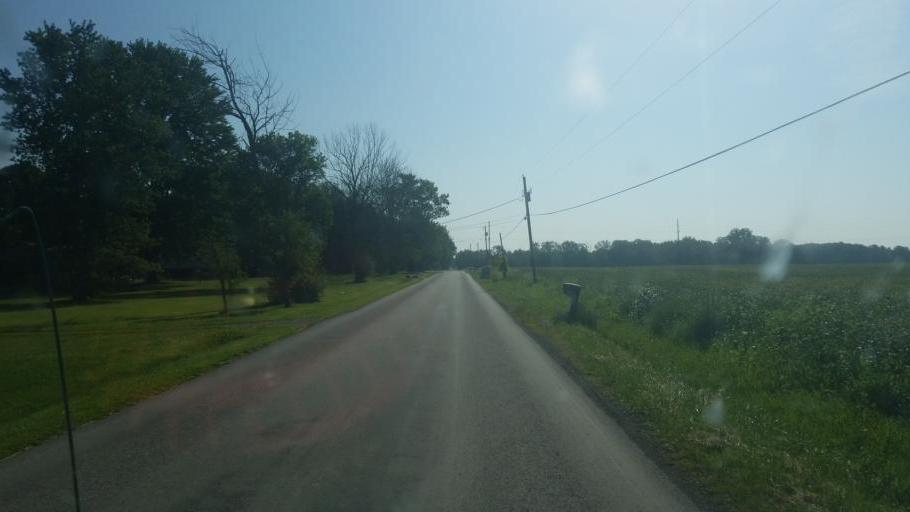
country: US
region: Ohio
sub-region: Wayne County
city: West Salem
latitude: 41.0855
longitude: -82.1264
